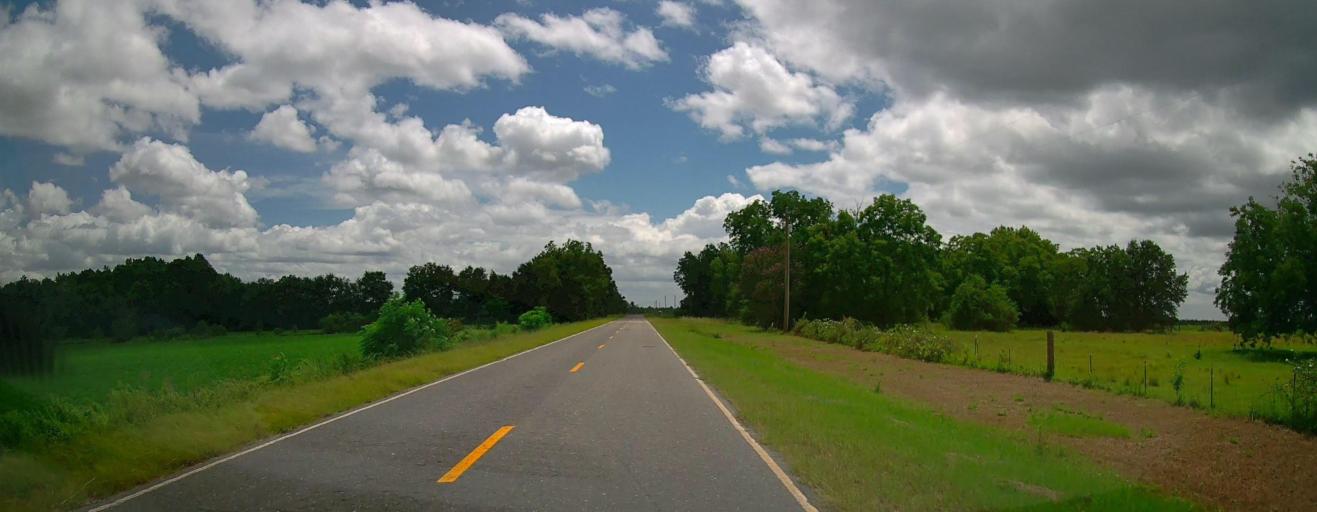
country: US
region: Georgia
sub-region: Ben Hill County
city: Fitzgerald
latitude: 31.6587
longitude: -83.4010
